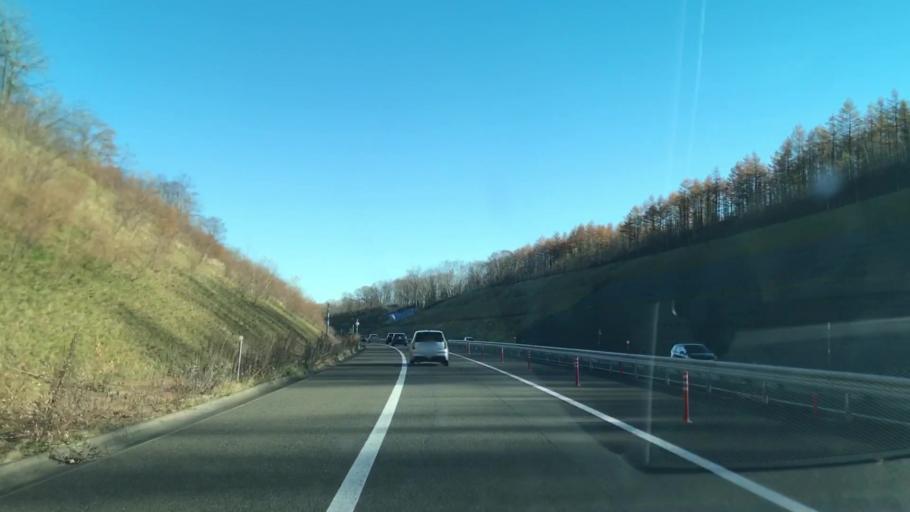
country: JP
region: Hokkaido
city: Otofuke
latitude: 43.0350
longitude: 142.7891
